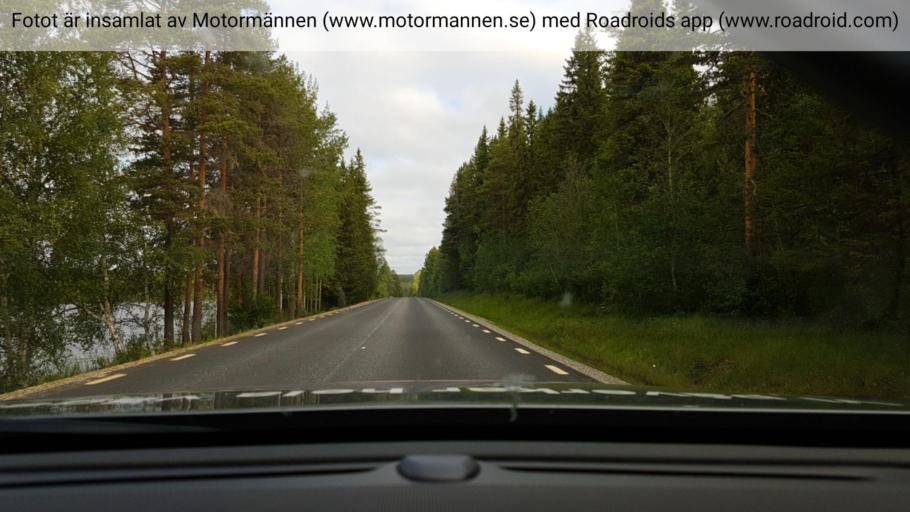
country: SE
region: Vaesterbotten
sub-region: Vindelns Kommun
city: Vindeln
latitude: 64.4390
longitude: 19.3454
